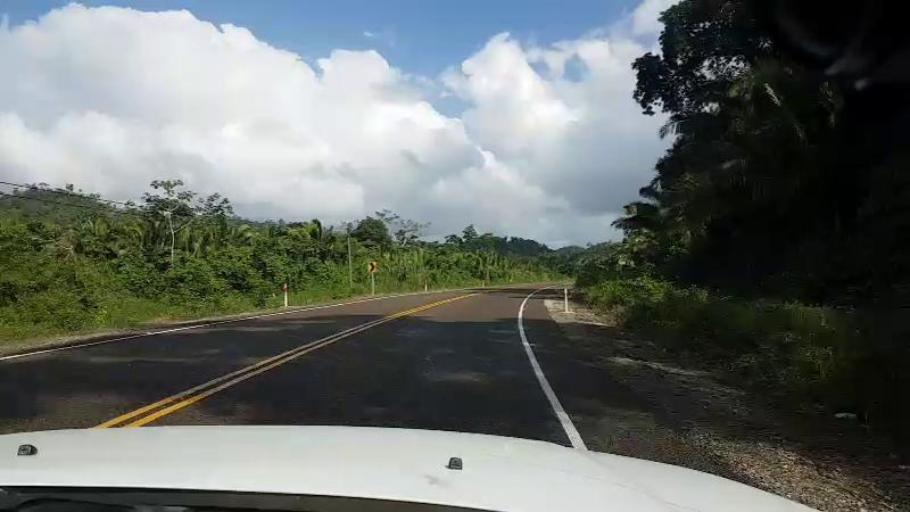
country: BZ
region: Cayo
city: Belmopan
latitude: 17.1483
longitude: -88.7242
